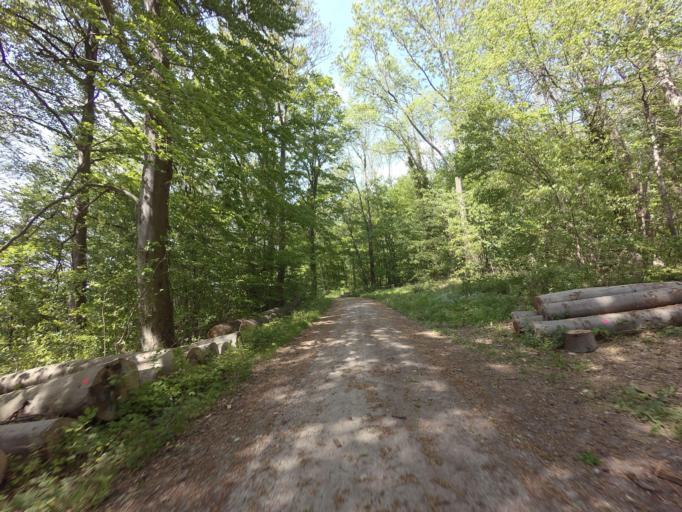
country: DE
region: Lower Saxony
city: Diekholzen
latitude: 52.1407
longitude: 9.8919
